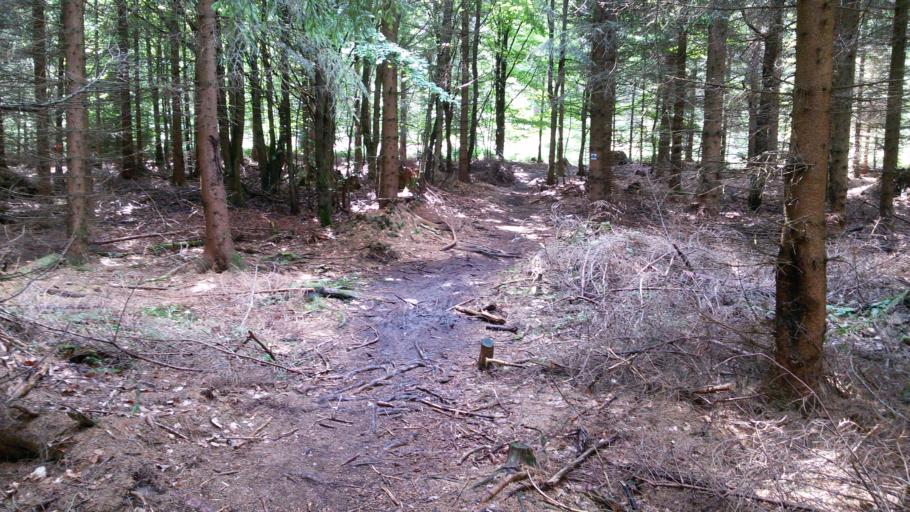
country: CZ
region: Vysocina
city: Heralec
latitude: 49.6438
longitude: 15.9992
